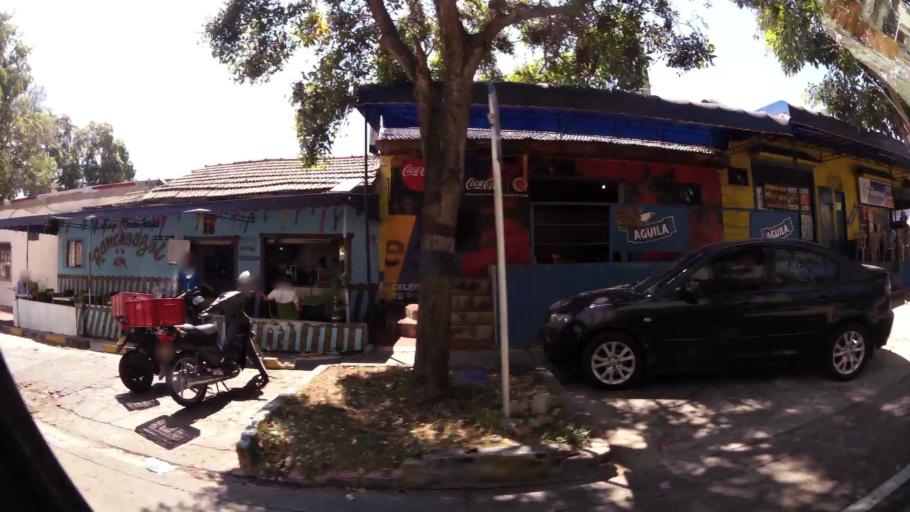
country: CO
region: Atlantico
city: Barranquilla
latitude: 10.9944
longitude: -74.7986
